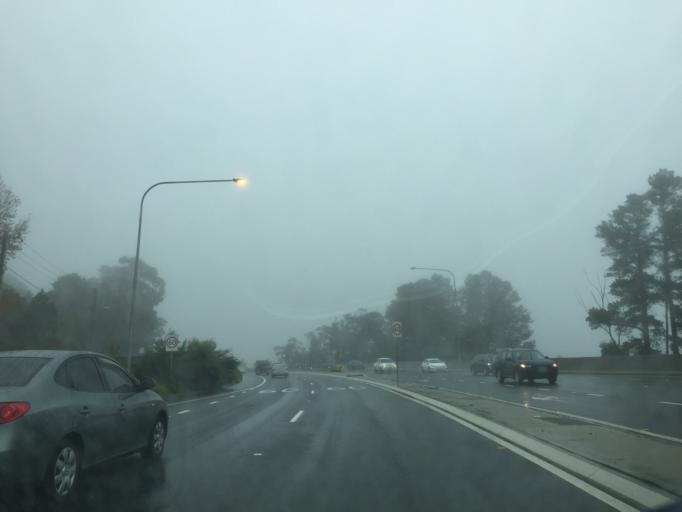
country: AU
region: New South Wales
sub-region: Blue Mountains Municipality
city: Lawson
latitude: -33.7167
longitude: 150.3827
